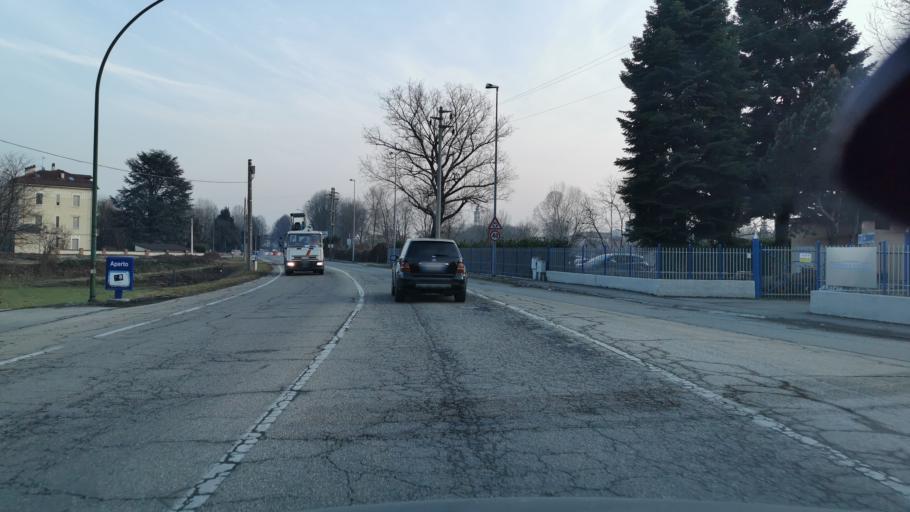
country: IT
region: Piedmont
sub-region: Provincia di Torino
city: Venaria Reale
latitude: 45.1399
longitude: 7.6263
